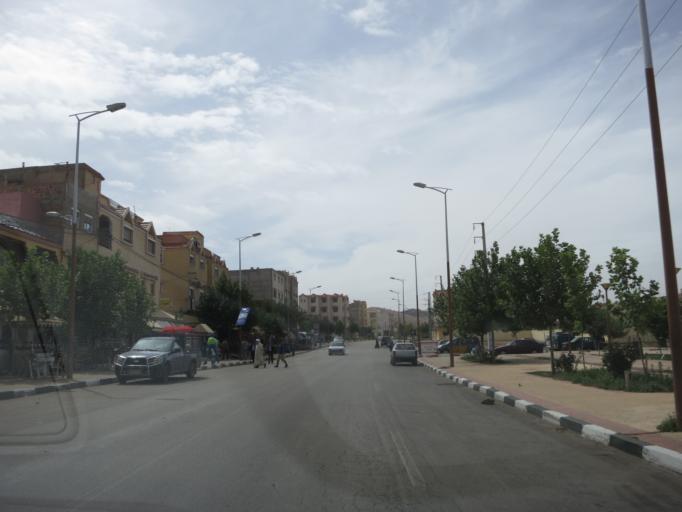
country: MA
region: Meknes-Tafilalet
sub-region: Ifrane
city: Azrou
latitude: 33.2356
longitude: -5.0587
